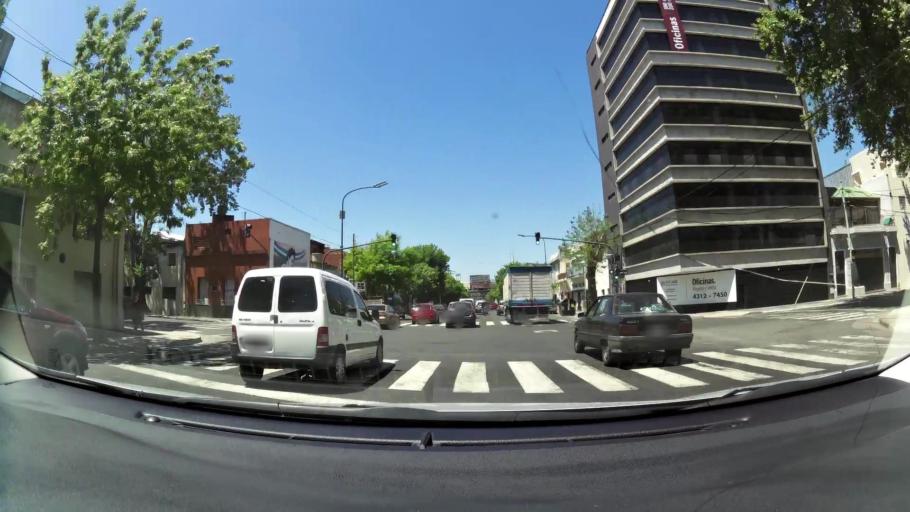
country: AR
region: Buenos Aires F.D.
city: Buenos Aires
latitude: -34.6393
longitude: -58.3975
